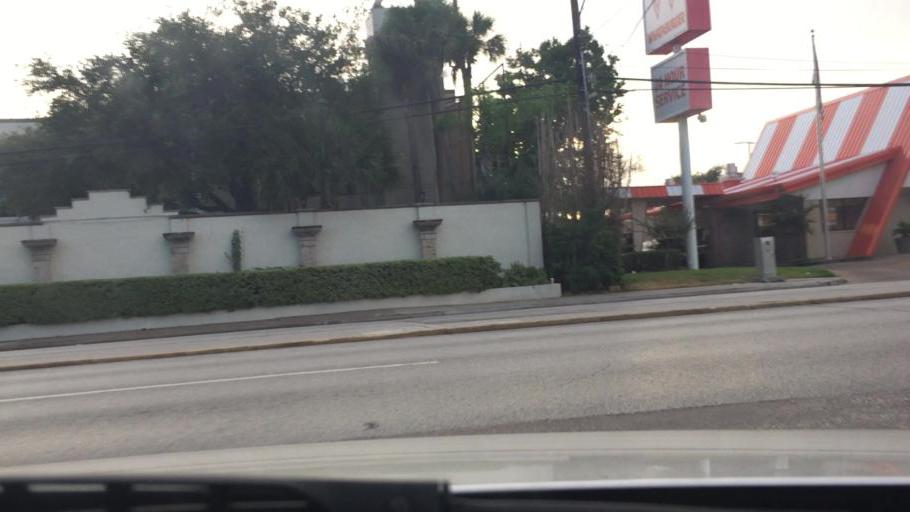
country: US
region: Texas
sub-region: Harris County
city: Bellaire
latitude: 29.7360
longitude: -95.4764
